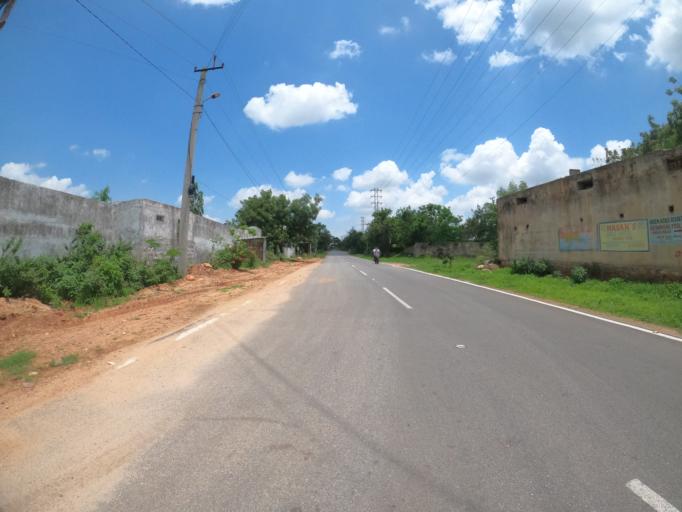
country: IN
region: Telangana
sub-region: Rangareddi
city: Sriramnagar
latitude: 17.3615
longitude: 78.3232
